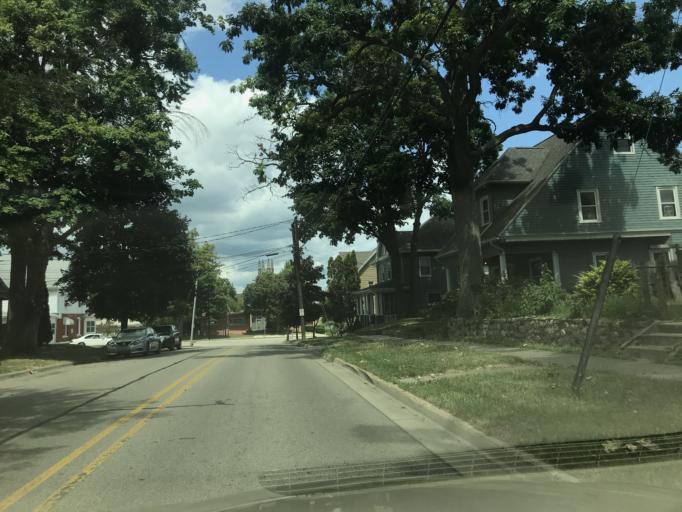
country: US
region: Michigan
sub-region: Jackson County
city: Jackson
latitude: 42.2466
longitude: -84.4185
